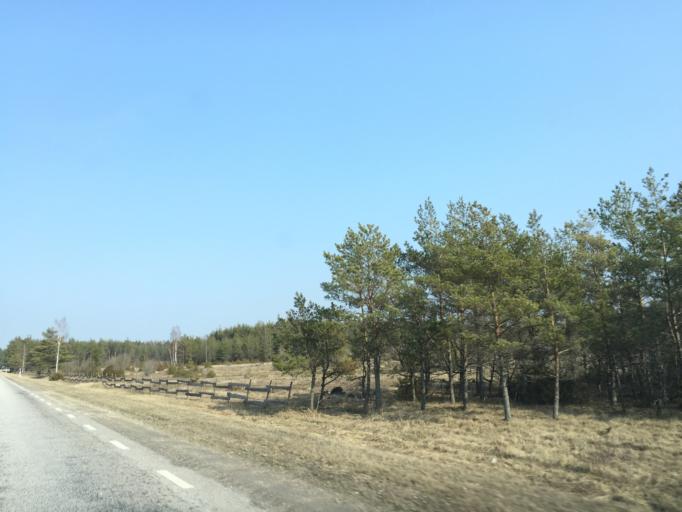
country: EE
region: Saare
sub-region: Kuressaare linn
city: Kuressaare
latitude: 58.3800
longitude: 22.7356
